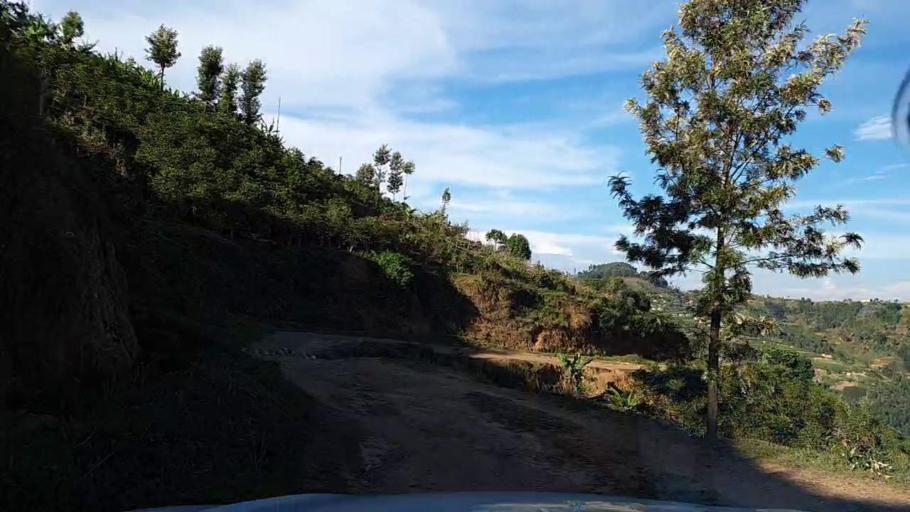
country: RW
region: Southern Province
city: Gikongoro
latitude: -2.4115
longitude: 29.5212
